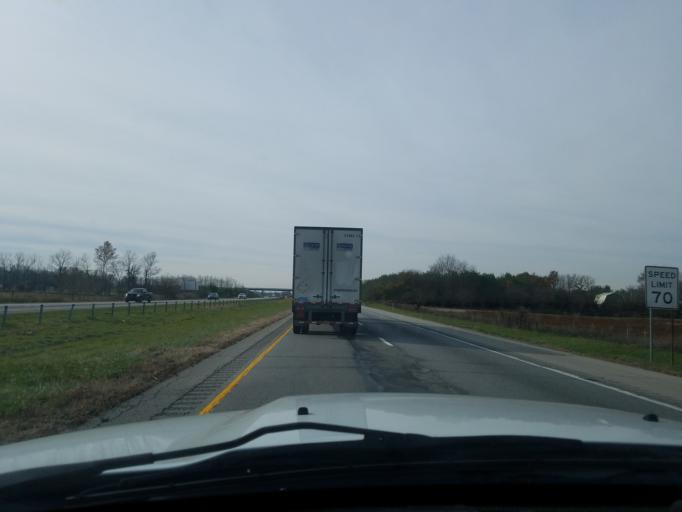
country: US
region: Indiana
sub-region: Madison County
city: Anderson
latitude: 40.0508
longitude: -85.6734
